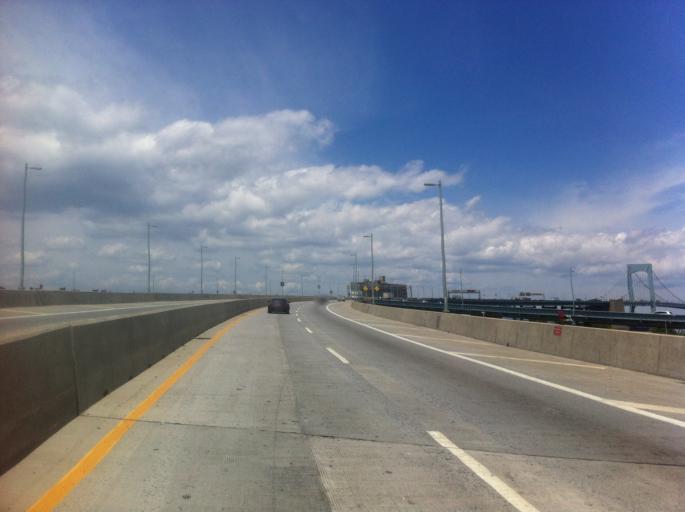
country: US
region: New York
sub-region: Nassau County
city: East Atlantic Beach
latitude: 40.7847
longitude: -73.7864
